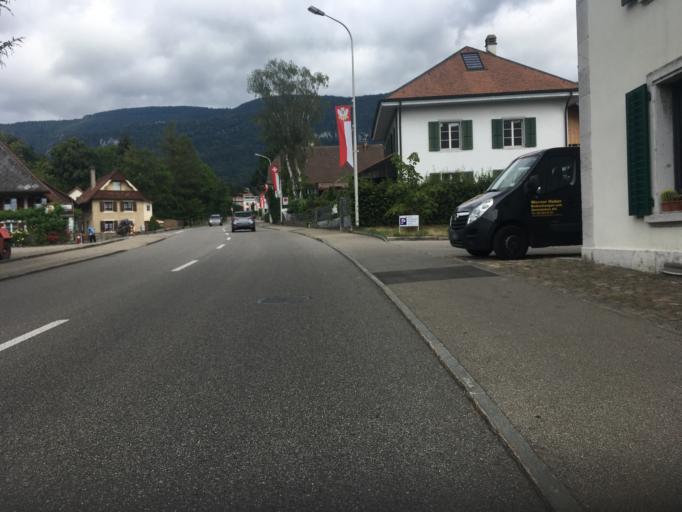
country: CH
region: Solothurn
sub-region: Bezirk Lebern
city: Langendorf
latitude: 47.2222
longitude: 7.5149
